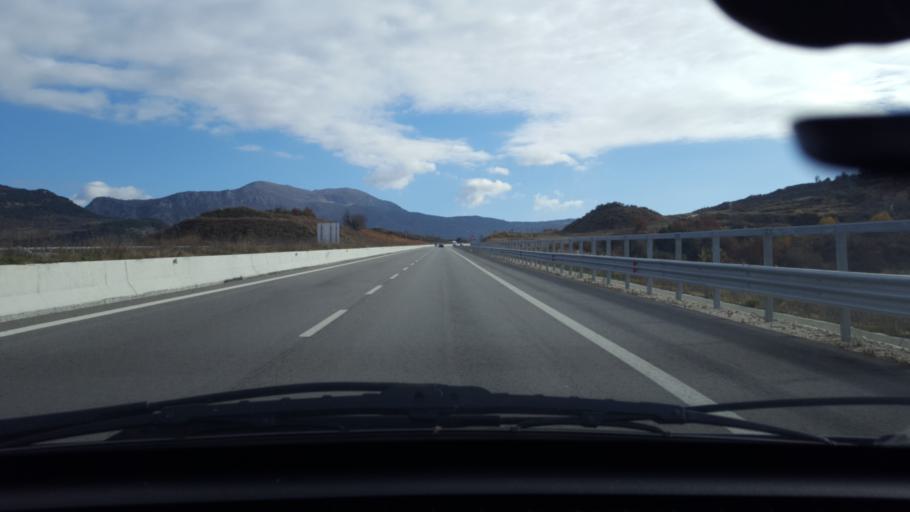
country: AL
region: Tirane
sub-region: Rrethi i Tiranes
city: Krrabe
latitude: 41.2258
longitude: 19.9376
